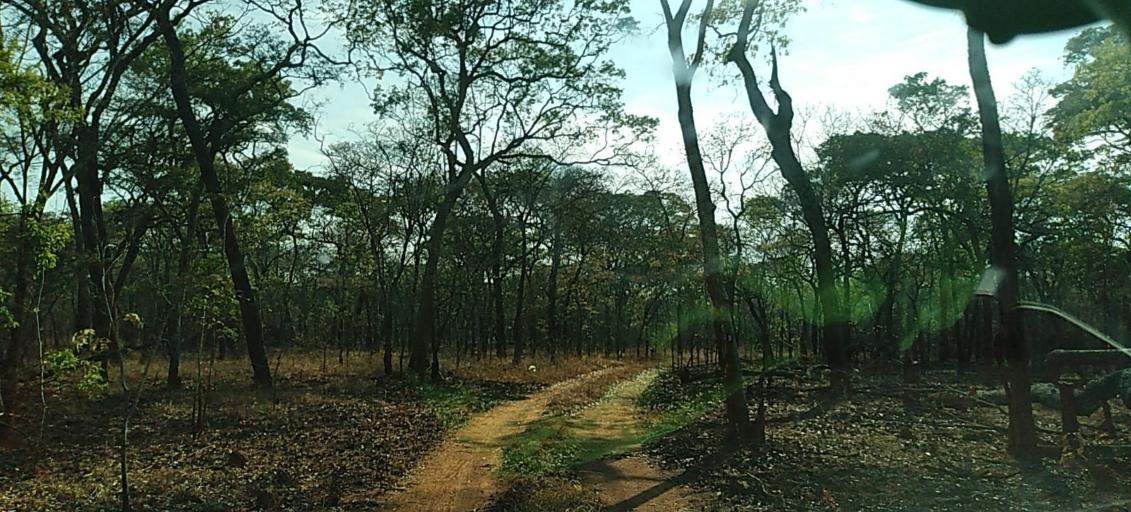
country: ZM
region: North-Western
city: Kalengwa
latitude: -13.2267
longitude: 25.0922
